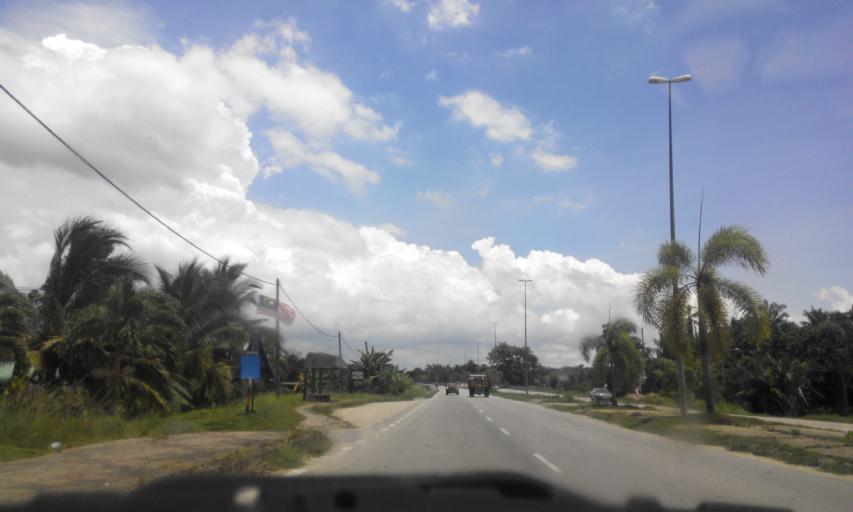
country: MY
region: Perak
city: Parit Buntar
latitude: 5.1207
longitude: 100.5201
